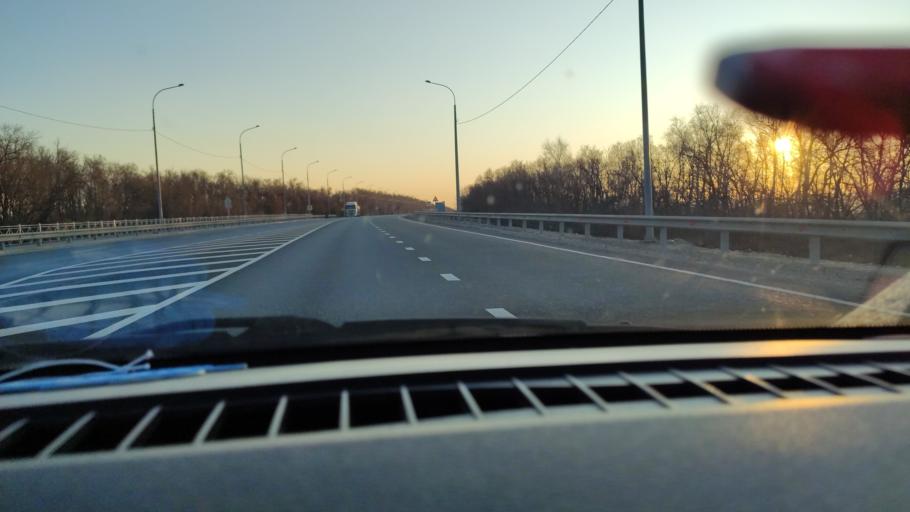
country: RU
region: Saratov
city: Yelshanka
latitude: 51.8957
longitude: 46.5308
